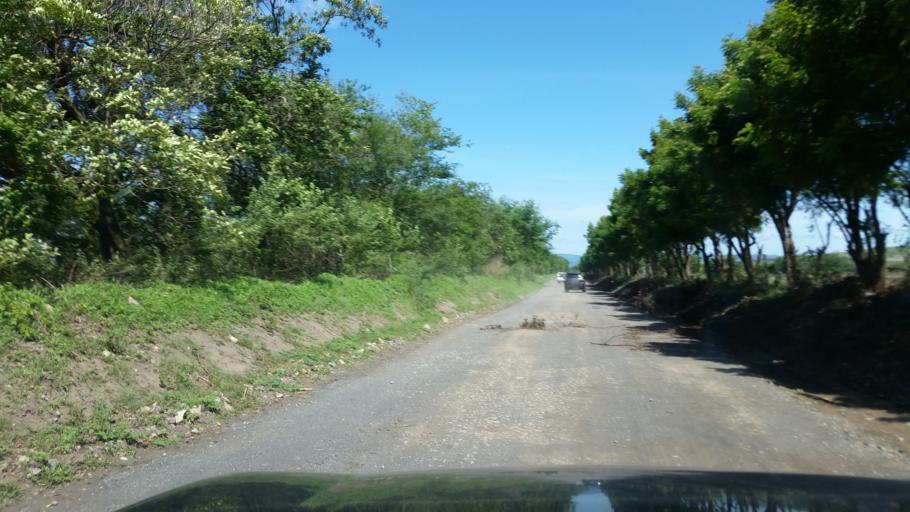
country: NI
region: Chinandega
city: Puerto Morazan
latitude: 12.7701
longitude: -87.0804
